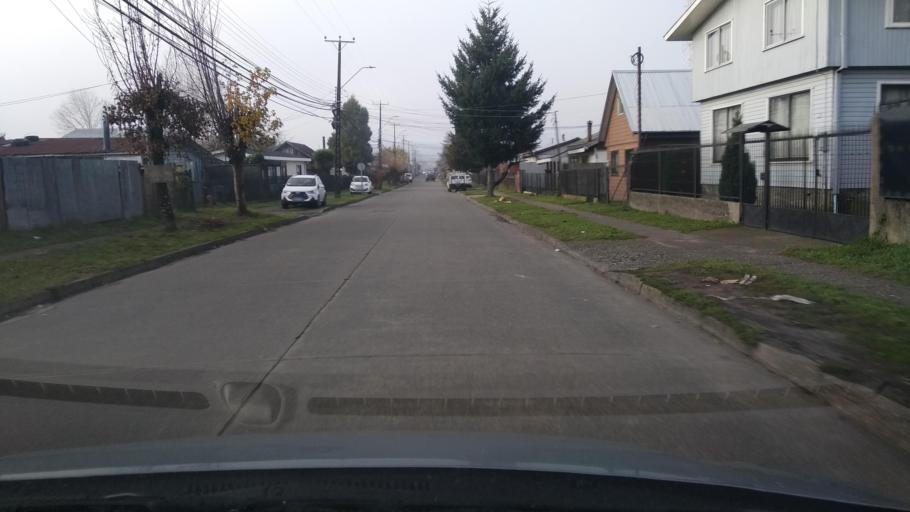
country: CL
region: Los Lagos
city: Las Animas
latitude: -39.8122
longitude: -73.2298
